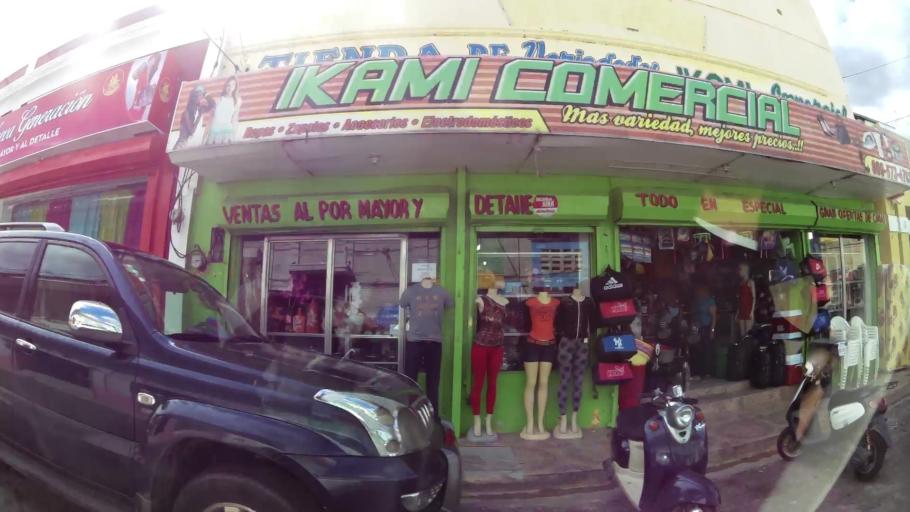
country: DO
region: La Vega
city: Concepcion de La Vega
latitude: 19.2257
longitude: -70.5299
